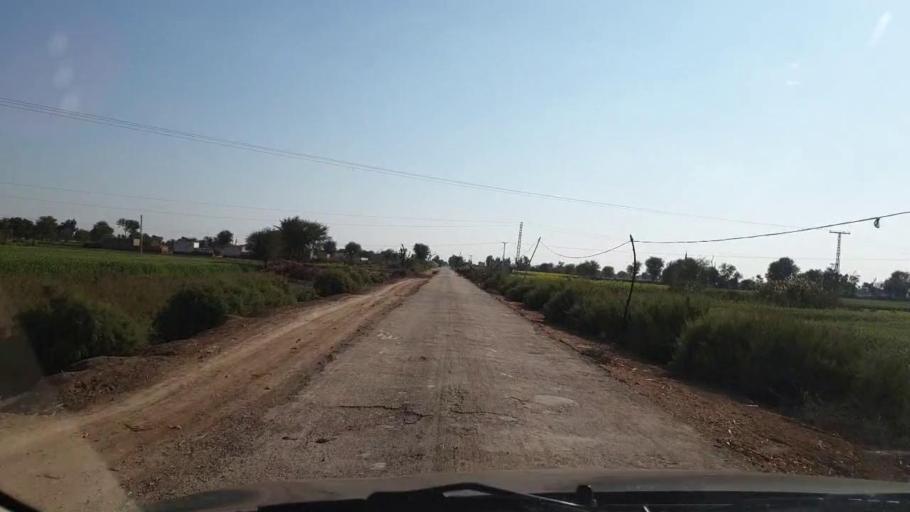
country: PK
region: Sindh
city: Sinjhoro
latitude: 25.9879
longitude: 68.8394
